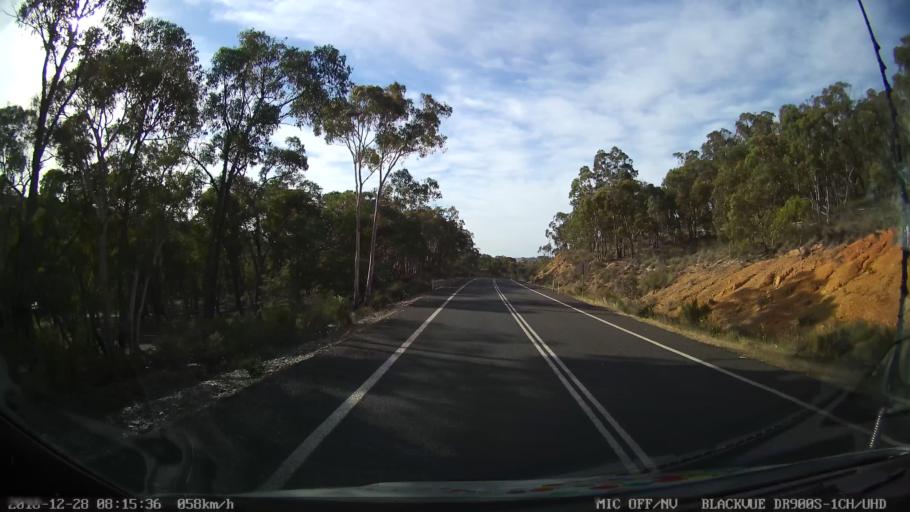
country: AU
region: New South Wales
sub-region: Blayney
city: Blayney
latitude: -33.8243
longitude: 149.3292
